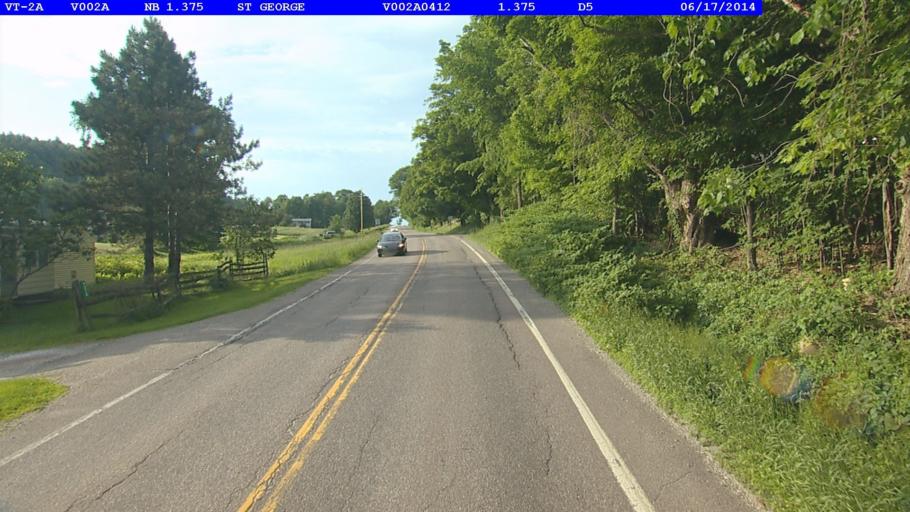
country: US
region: Vermont
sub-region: Chittenden County
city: Hinesburg
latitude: 44.3893
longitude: -73.1274
